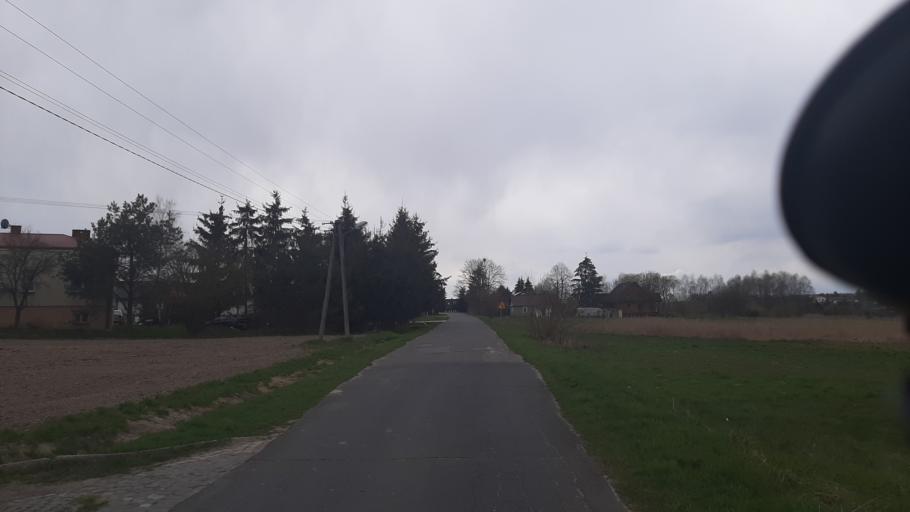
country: PL
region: Lublin Voivodeship
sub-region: Powiat lubelski
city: Niemce
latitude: 51.3654
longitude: 22.5466
